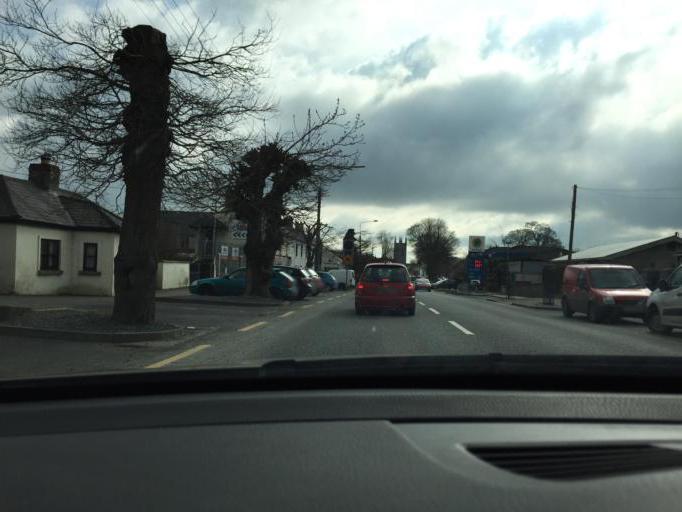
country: IE
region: Leinster
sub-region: Wicklow
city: Blessington
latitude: 53.1738
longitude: -6.5289
